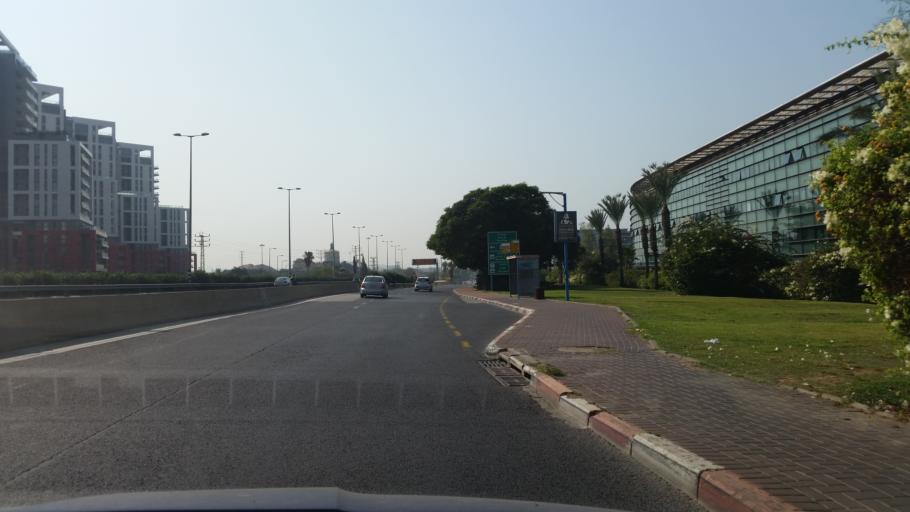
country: IL
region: Tel Aviv
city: Herzliyya
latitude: 32.1644
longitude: 34.8132
